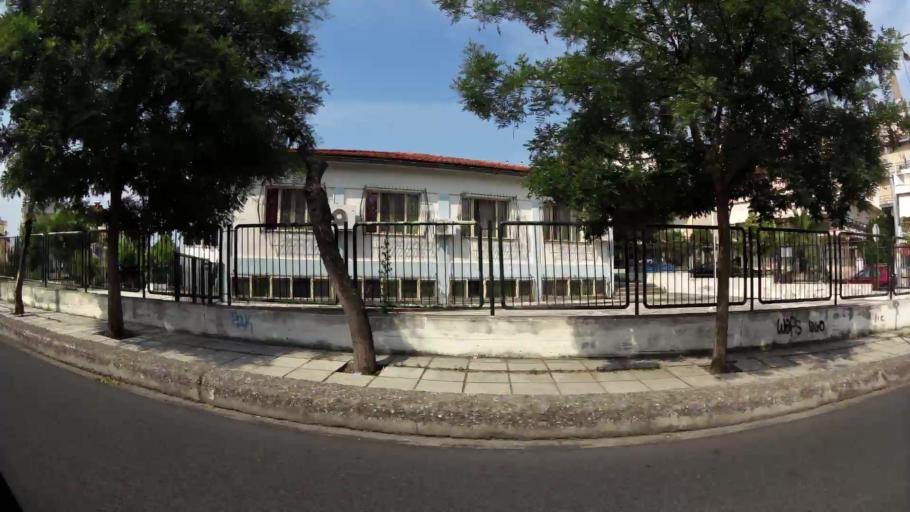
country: GR
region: Central Macedonia
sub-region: Nomos Thessalonikis
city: Agios Pavlos
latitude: 40.6485
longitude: 22.9599
